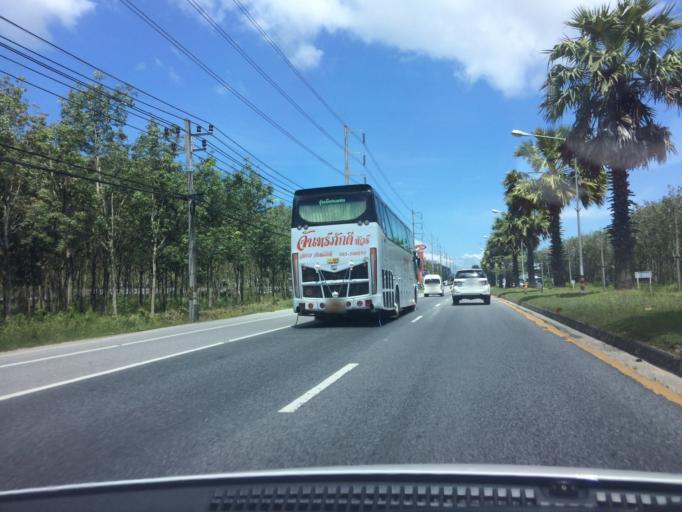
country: TH
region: Phuket
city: Thalang
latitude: 8.0606
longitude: 98.3407
